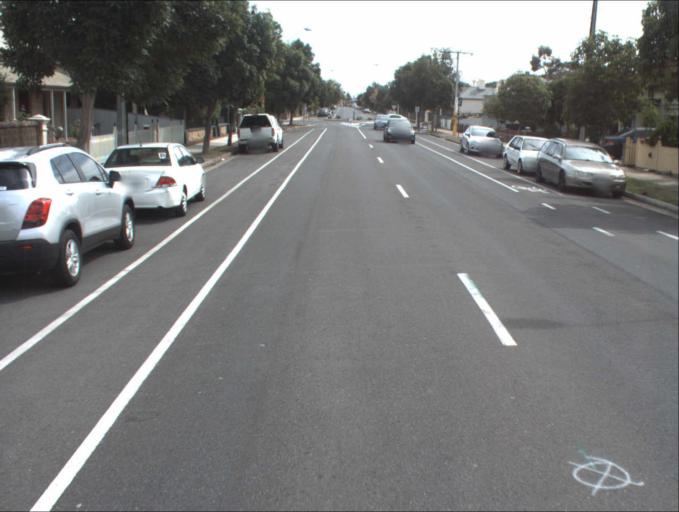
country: AU
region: South Australia
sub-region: Port Adelaide Enfield
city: Birkenhead
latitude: -34.8358
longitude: 138.4883
